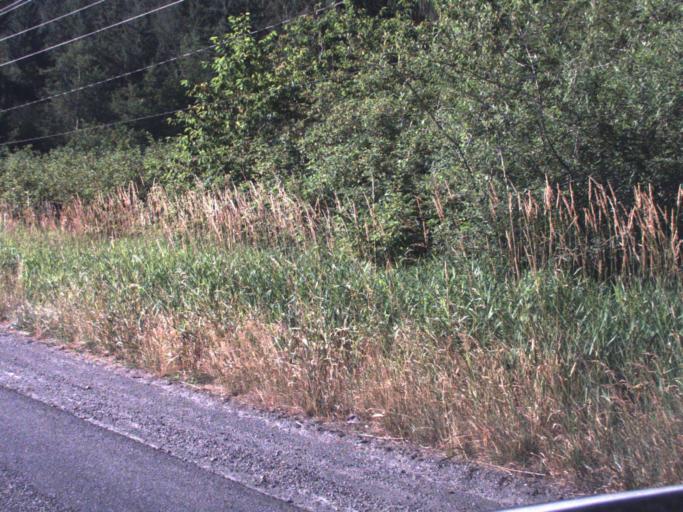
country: US
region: Washington
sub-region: King County
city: Enumclaw
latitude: 47.1905
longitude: -121.9326
